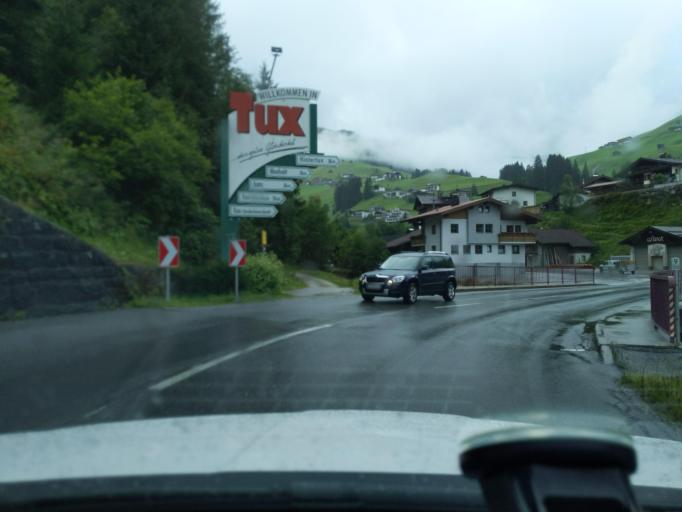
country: AT
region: Tyrol
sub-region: Politischer Bezirk Schwaz
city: Schwendau
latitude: 47.1609
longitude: 11.7476
